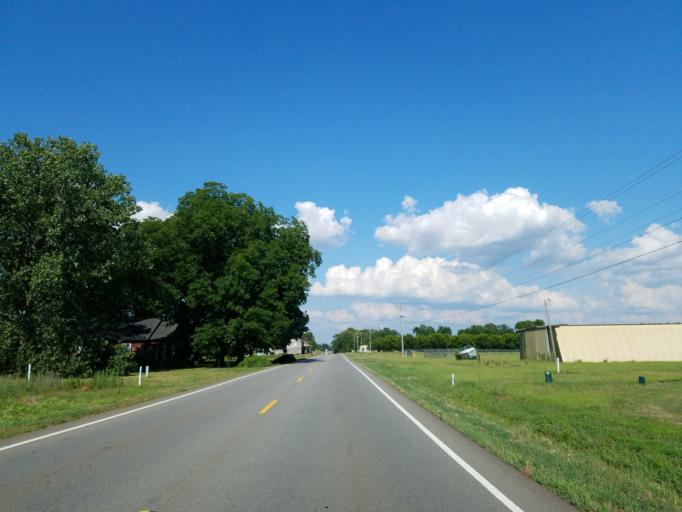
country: US
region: Georgia
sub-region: Peach County
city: Fort Valley
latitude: 32.5538
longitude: -83.8017
